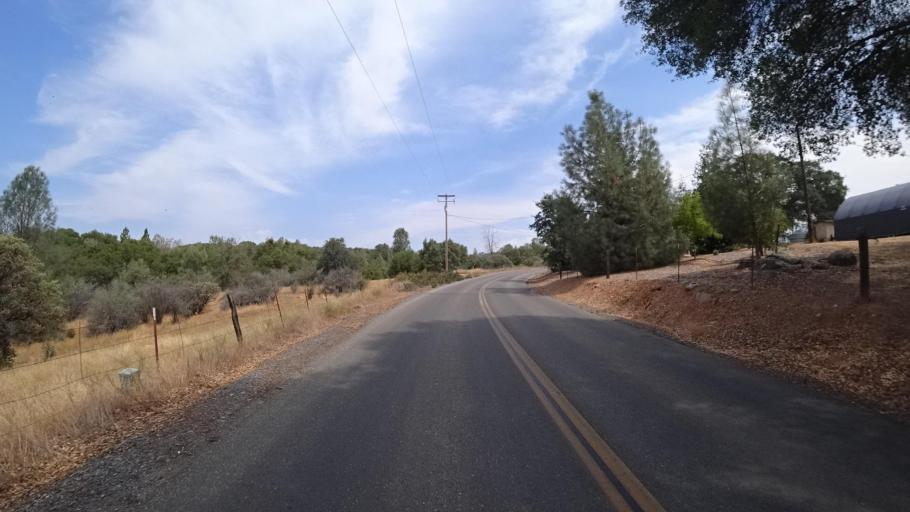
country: US
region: California
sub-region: Mariposa County
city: Midpines
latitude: 37.4772
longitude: -119.8870
